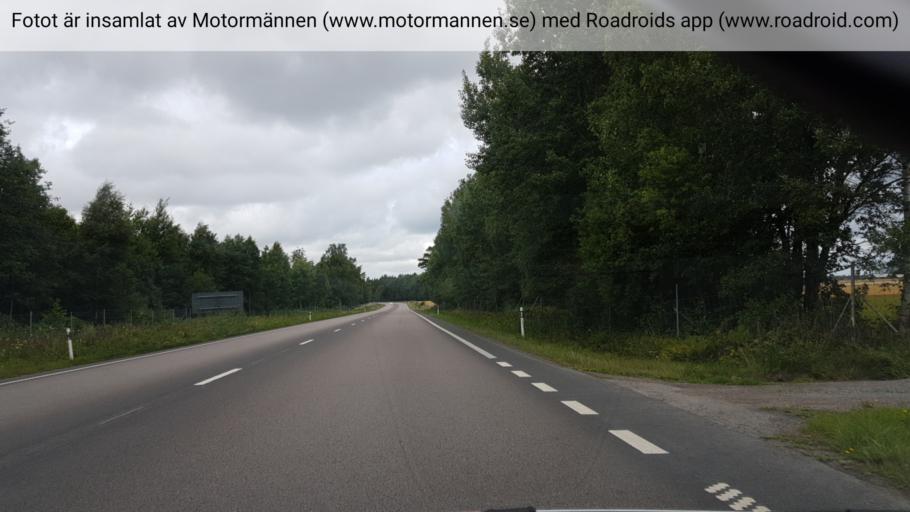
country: SE
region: Vaestra Goetaland
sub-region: Lidkopings Kommun
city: Vinninga
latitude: 58.4507
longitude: 13.2417
